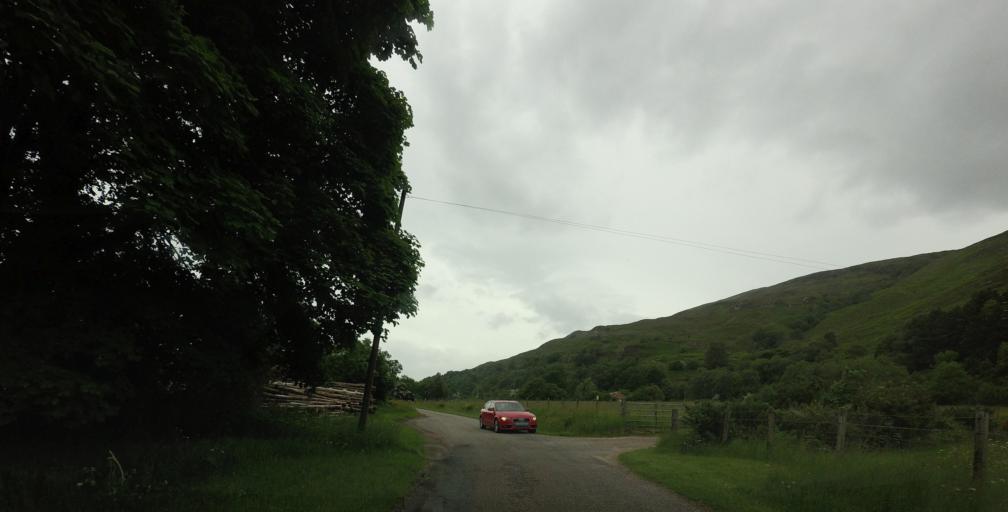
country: GB
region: Scotland
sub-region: Highland
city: Fort William
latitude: 56.8203
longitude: -5.1334
